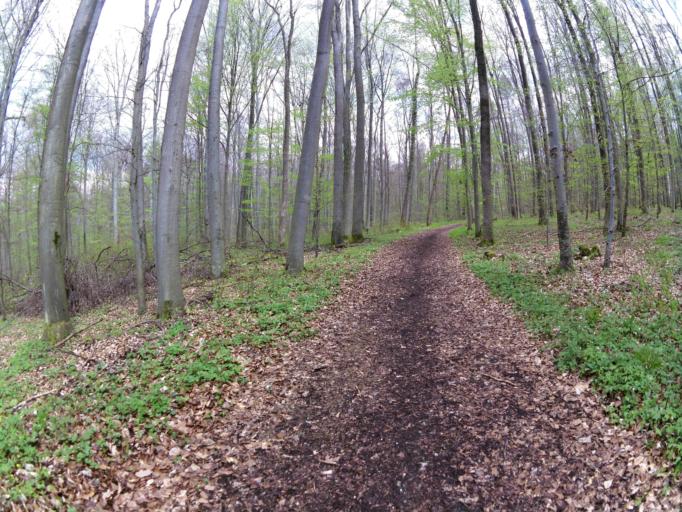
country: DE
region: Bavaria
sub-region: Regierungsbezirk Unterfranken
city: Hettstadt
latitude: 49.7907
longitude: 9.7869
